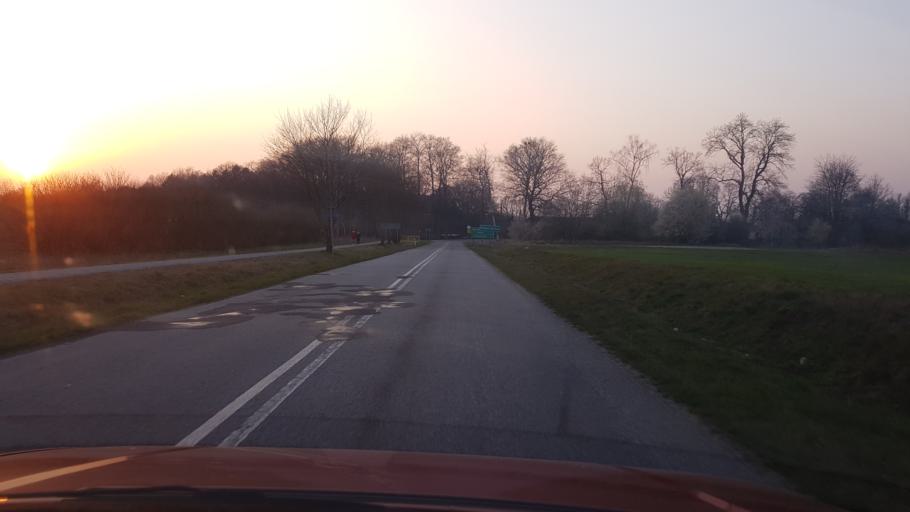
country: PL
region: West Pomeranian Voivodeship
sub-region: Powiat lobeski
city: Radowo Male
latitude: 53.6821
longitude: 15.4239
